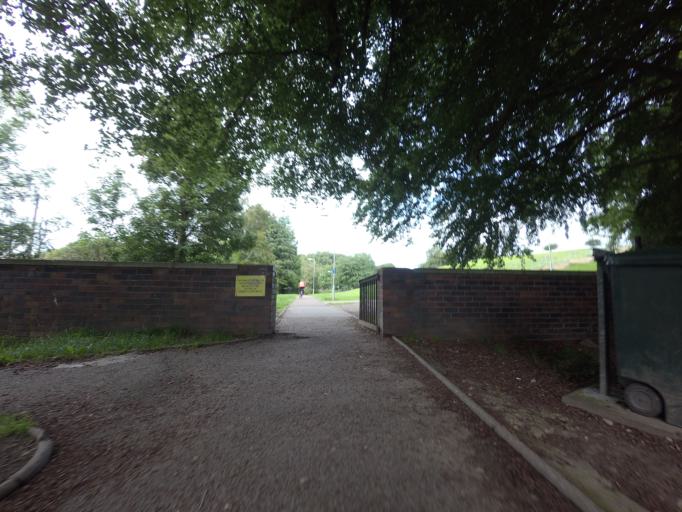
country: GB
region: Scotland
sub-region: Moray
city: Elgin
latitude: 57.6510
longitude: -3.3260
